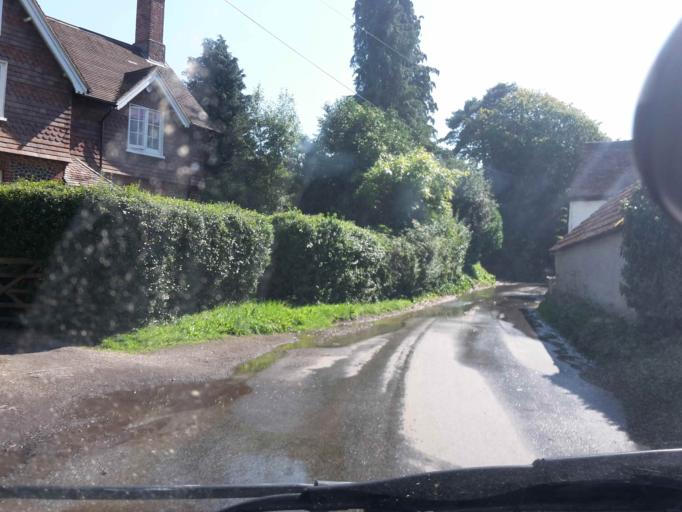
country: GB
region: England
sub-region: Surrey
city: Cranleigh
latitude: 51.1949
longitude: -0.4828
